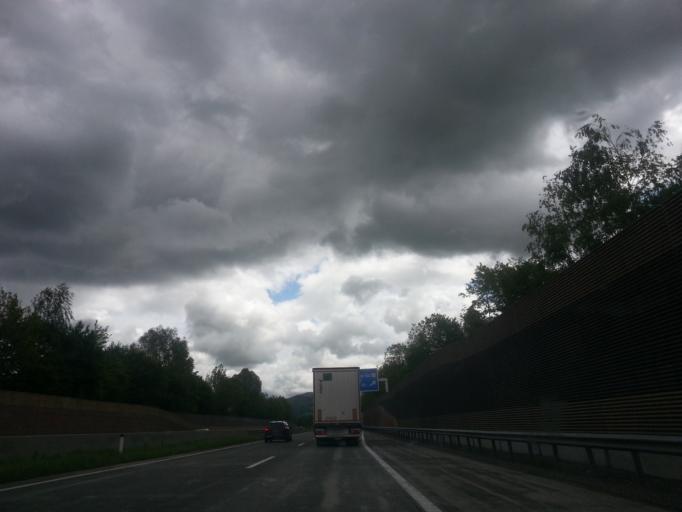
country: AT
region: Salzburg
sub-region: Politischer Bezirk Salzburg-Umgebung
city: Grodig
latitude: 47.7426
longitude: 13.0429
